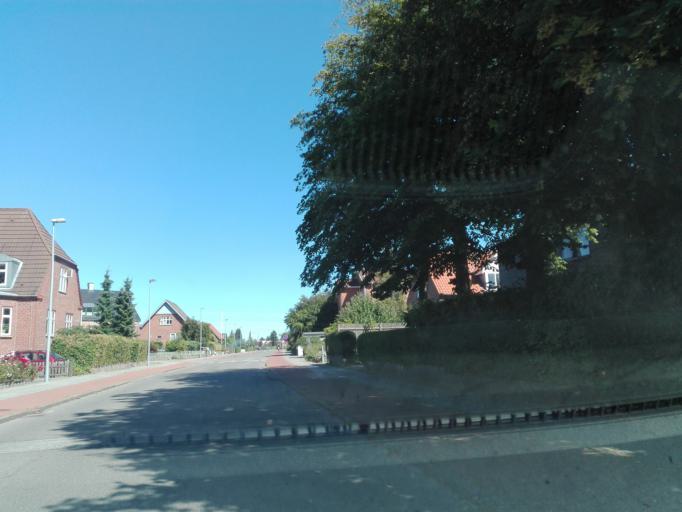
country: DK
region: Central Jutland
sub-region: Odder Kommune
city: Odder
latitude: 55.9752
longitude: 10.1602
